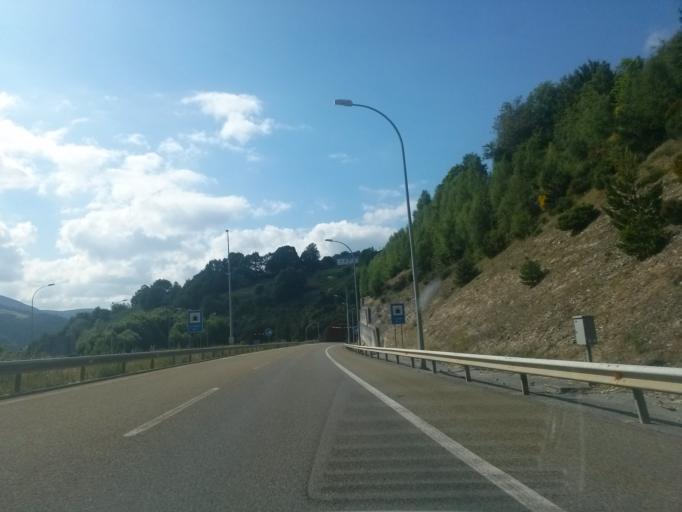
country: ES
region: Castille and Leon
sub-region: Provincia de Leon
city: Balboa
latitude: 42.7318
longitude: -7.0438
